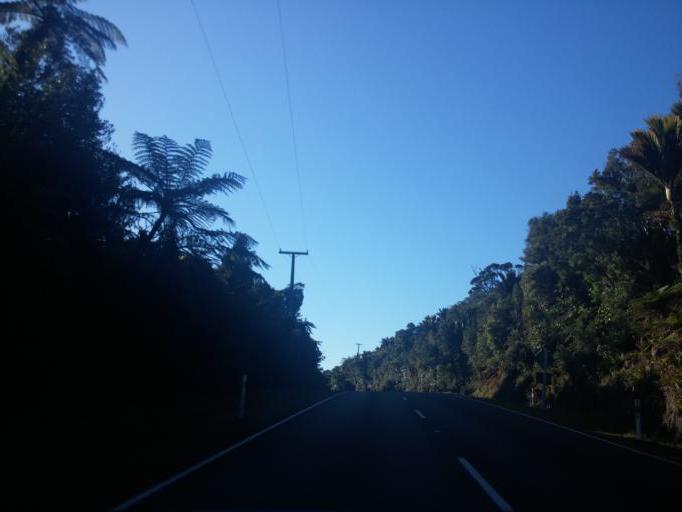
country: NZ
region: West Coast
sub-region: Grey District
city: Greymouth
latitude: -42.0965
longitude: 171.3433
